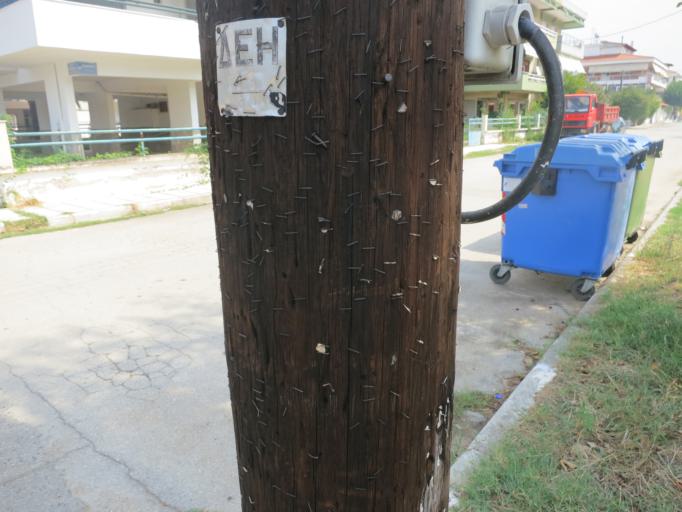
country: GR
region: Central Macedonia
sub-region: Nomos Chalkidikis
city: Nea Flogita
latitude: 40.2508
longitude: 23.2497
